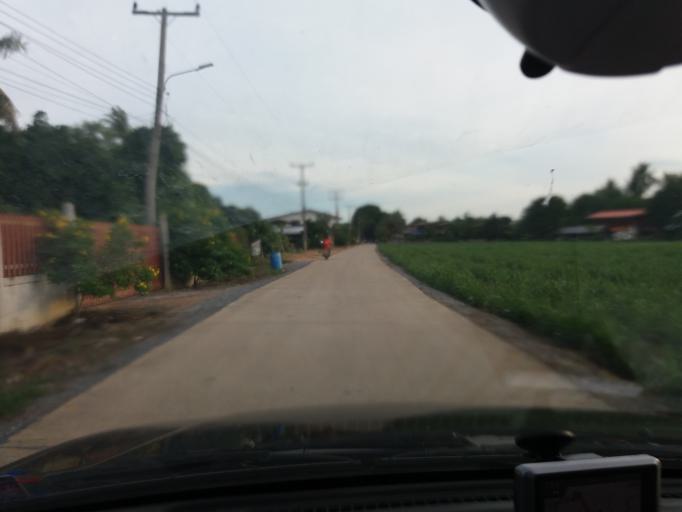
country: TH
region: Suphan Buri
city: Doembang Nangbuat
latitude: 14.8193
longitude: 100.1376
